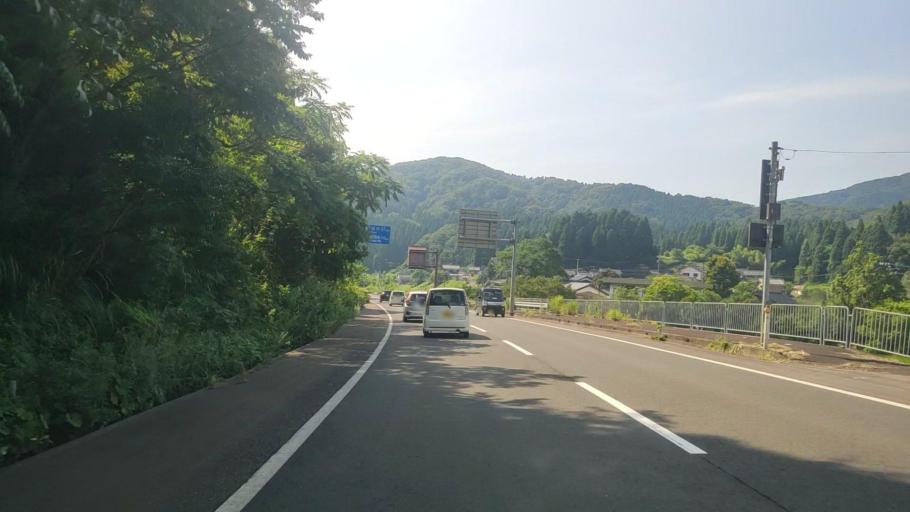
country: JP
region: Fukui
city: Tsuruga
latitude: 35.6083
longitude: 136.1198
